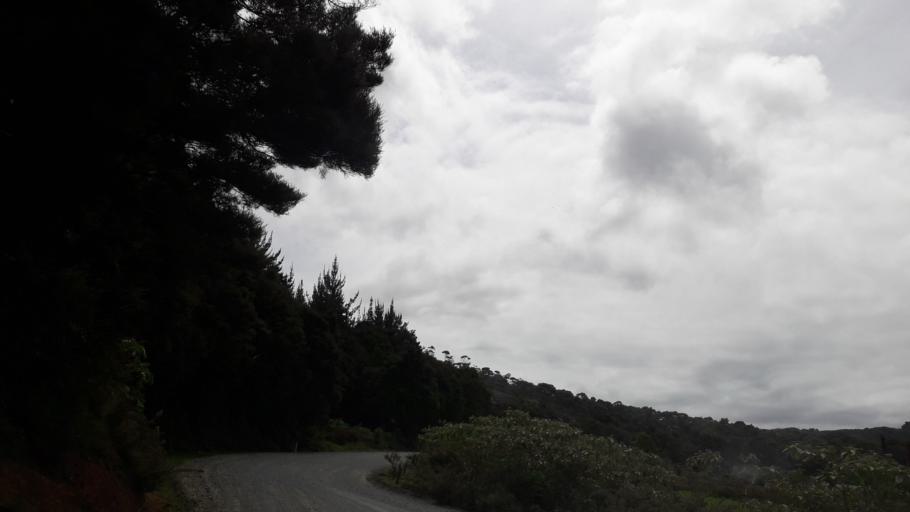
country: NZ
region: Northland
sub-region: Far North District
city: Taipa
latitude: -35.0381
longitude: 173.5657
